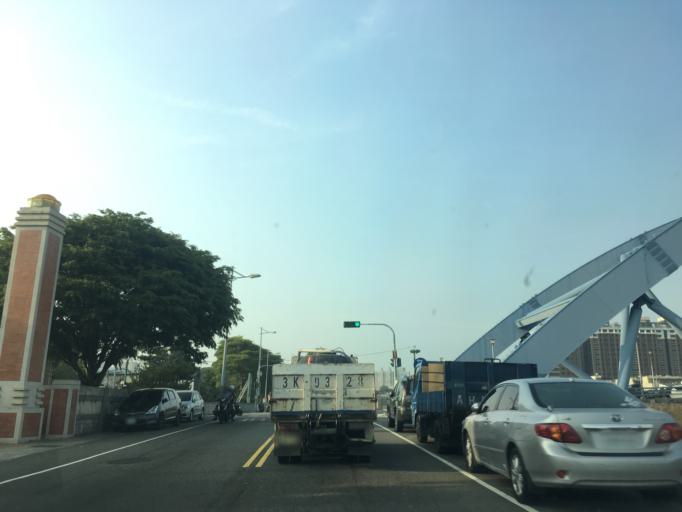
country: TW
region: Taiwan
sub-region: Taichung City
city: Taichung
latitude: 24.1591
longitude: 120.7039
